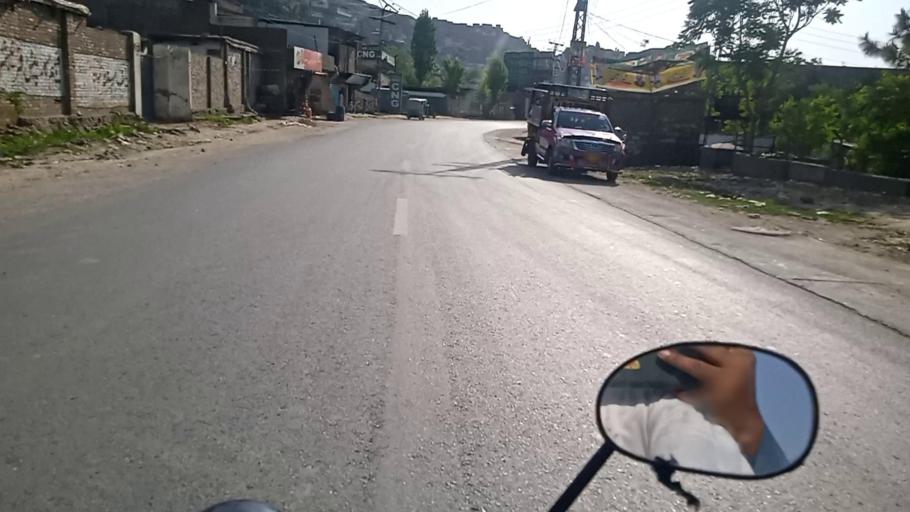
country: PK
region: Khyber Pakhtunkhwa
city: Saidu Sharif
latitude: 34.7589
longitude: 72.3167
